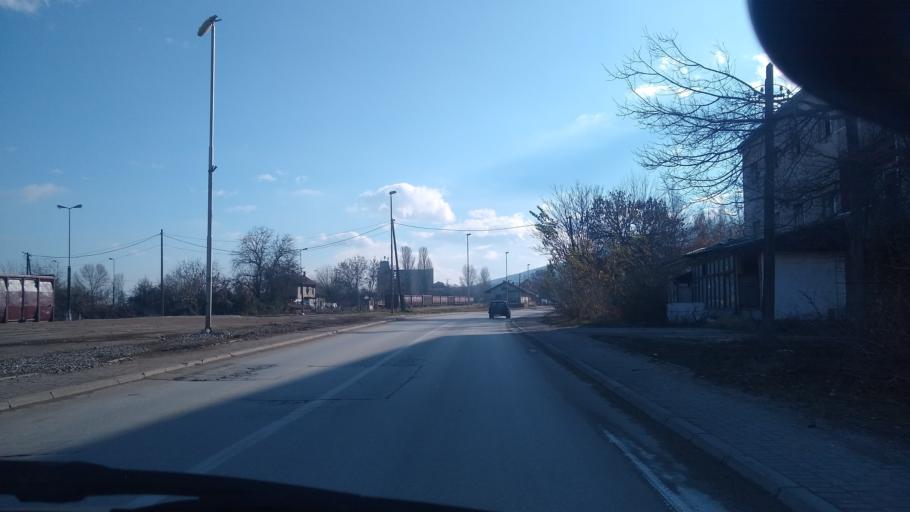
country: MK
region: Bitola
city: Bitola
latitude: 41.0226
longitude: 21.3421
